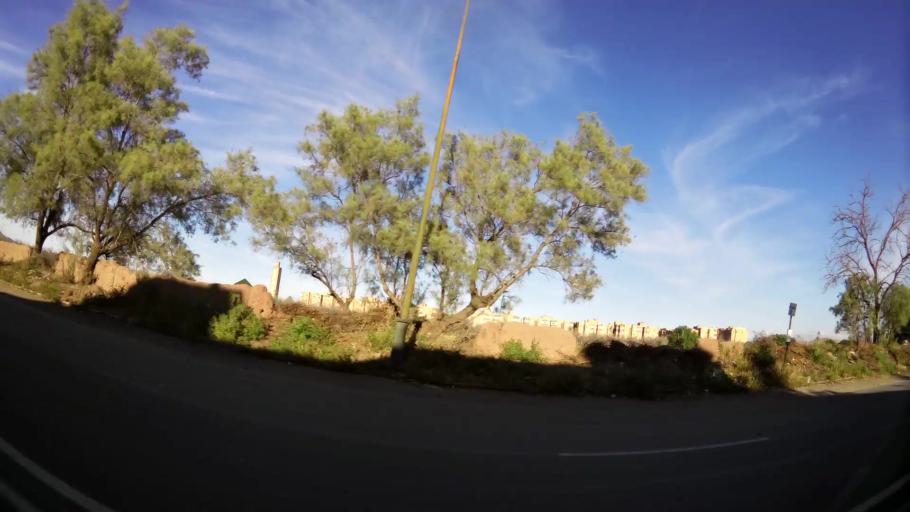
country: MA
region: Marrakech-Tensift-Al Haouz
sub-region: Marrakech
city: Marrakesh
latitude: 31.6727
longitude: -8.0587
